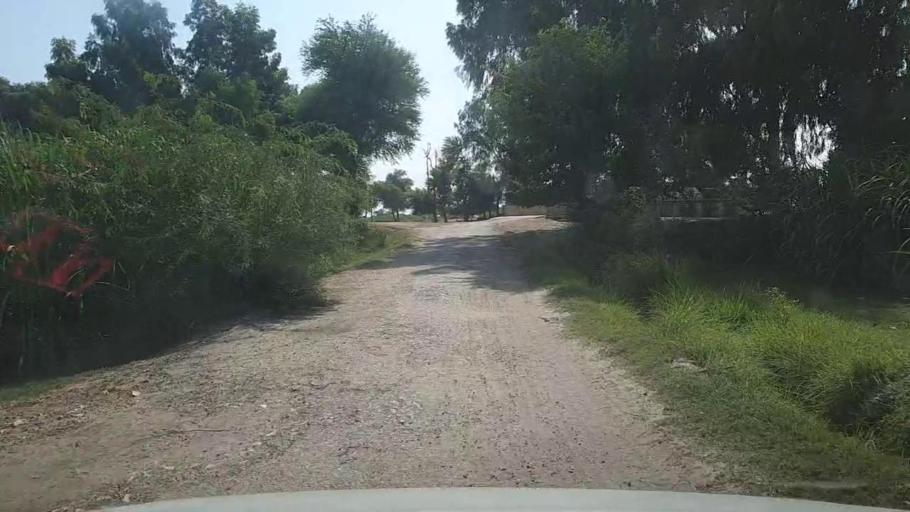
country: PK
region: Sindh
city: Mirpur Mathelo
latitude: 28.1192
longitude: 69.5980
